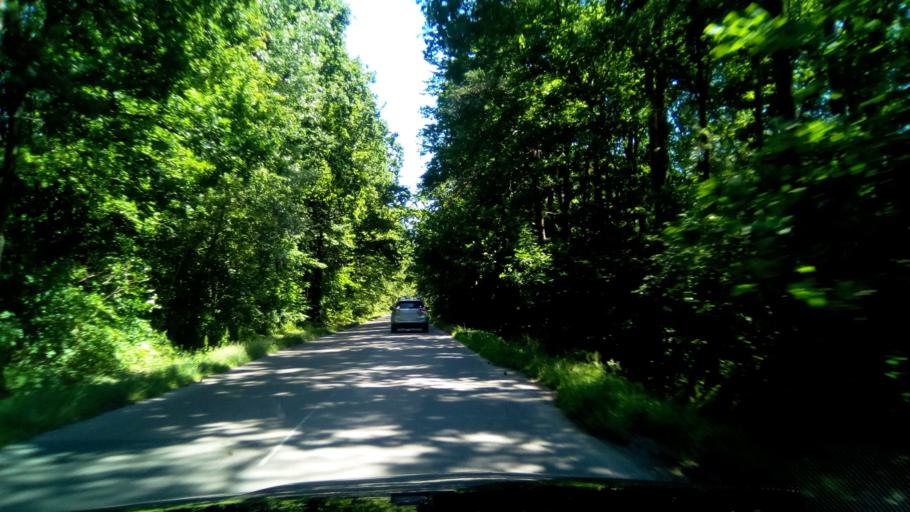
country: PL
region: Masovian Voivodeship
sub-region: Radom
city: Radom
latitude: 51.4308
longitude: 21.1288
